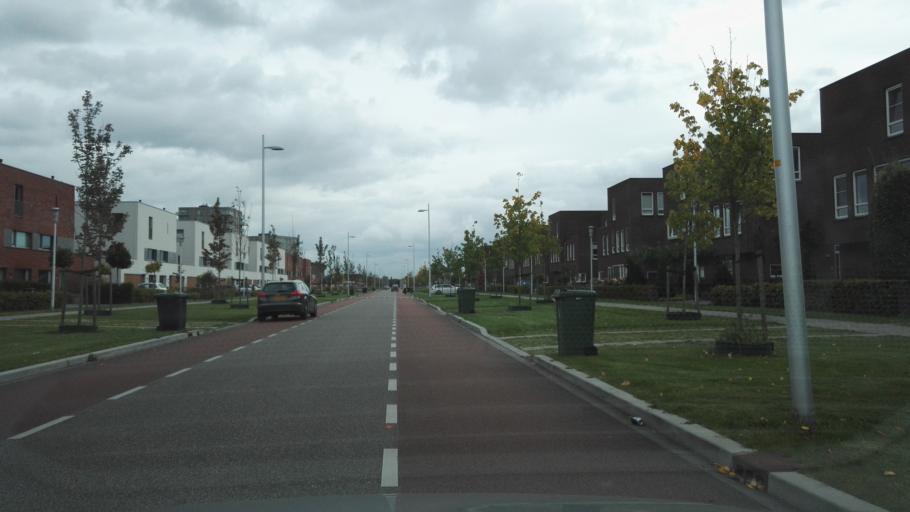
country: NL
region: Gelderland
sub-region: Gemeente Apeldoorn
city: Apeldoorn
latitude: 52.2362
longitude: 5.9915
